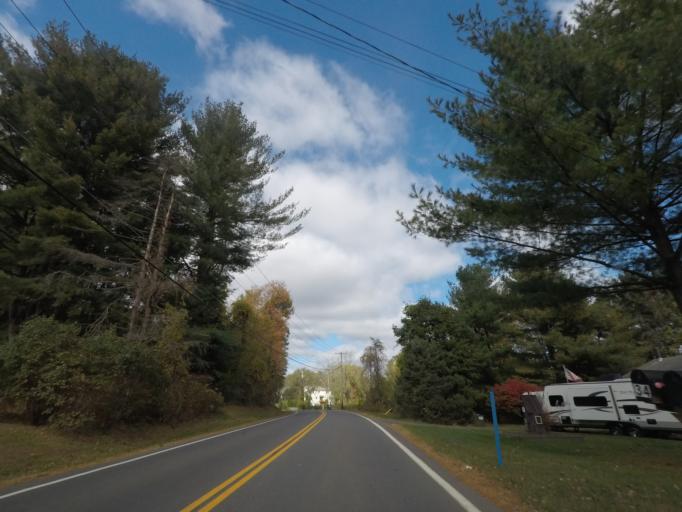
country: US
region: New York
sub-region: Albany County
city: Cohoes
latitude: 42.8277
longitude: -73.7473
